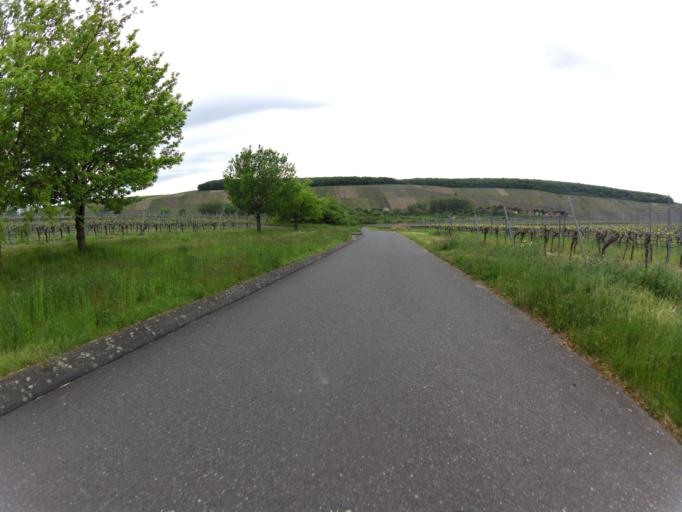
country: DE
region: Bavaria
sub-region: Regierungsbezirk Unterfranken
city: Nordheim
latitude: 49.8468
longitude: 10.1802
